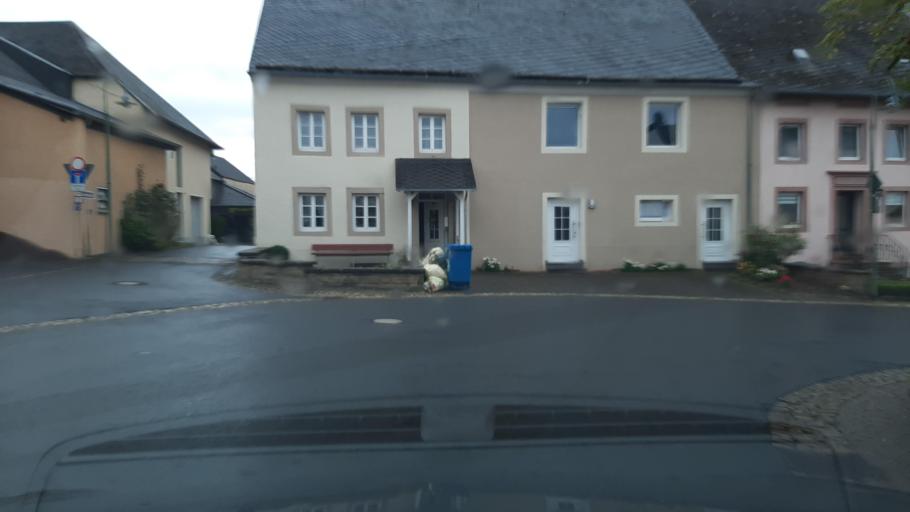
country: DE
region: Rheinland-Pfalz
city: Metterich
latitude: 49.9787
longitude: 6.5878
